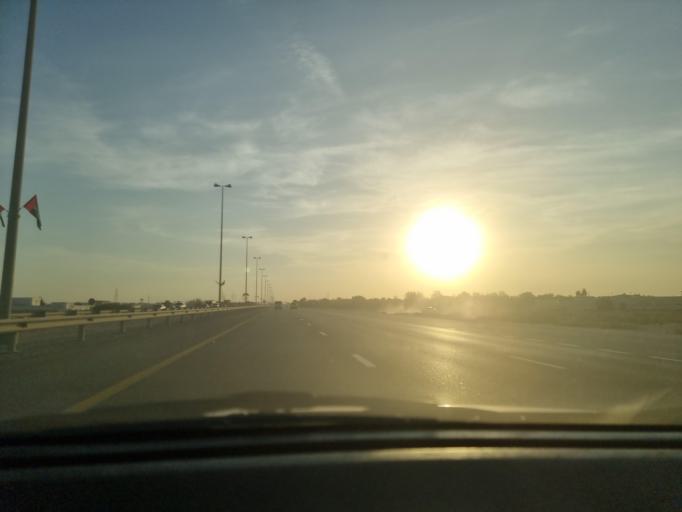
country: AE
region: Abu Dhabi
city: Abu Dhabi
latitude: 24.3089
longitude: 54.6729
